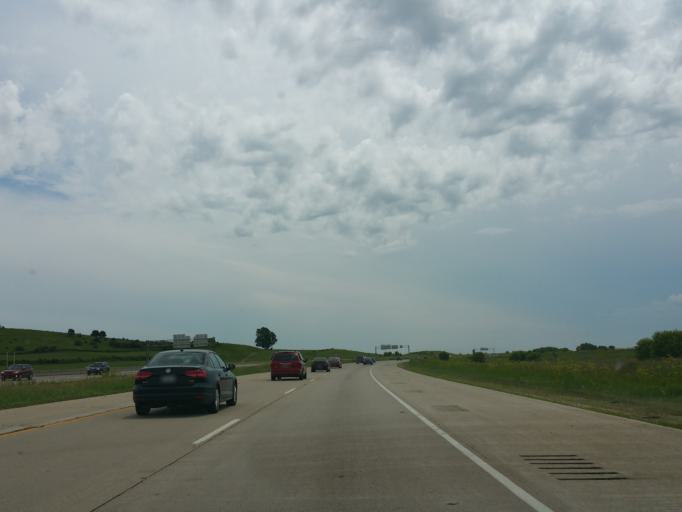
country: US
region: Wisconsin
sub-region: Columbia County
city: Portage
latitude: 43.4862
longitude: -89.4930
